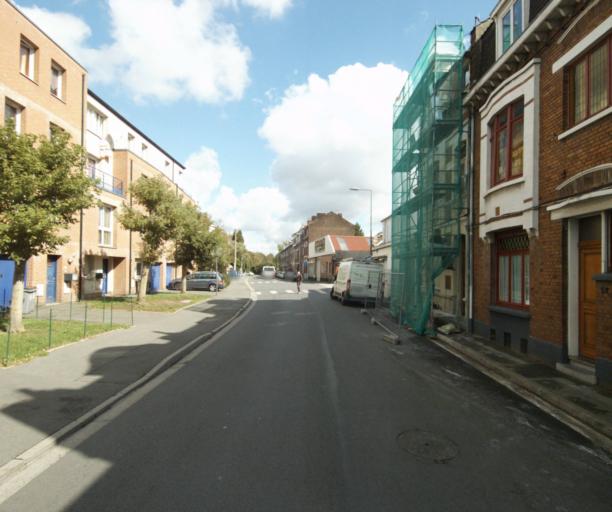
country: FR
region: Nord-Pas-de-Calais
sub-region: Departement du Nord
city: Loos
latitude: 50.6164
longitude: 3.0289
